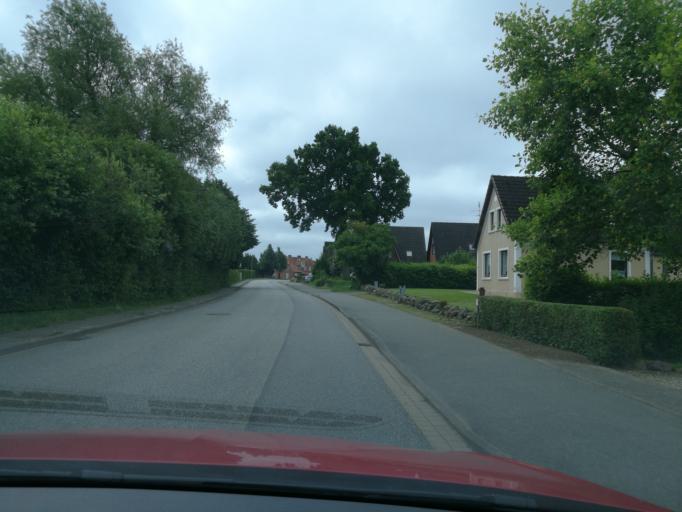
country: DE
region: Schleswig-Holstein
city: Politz
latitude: 53.7954
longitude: 10.3837
